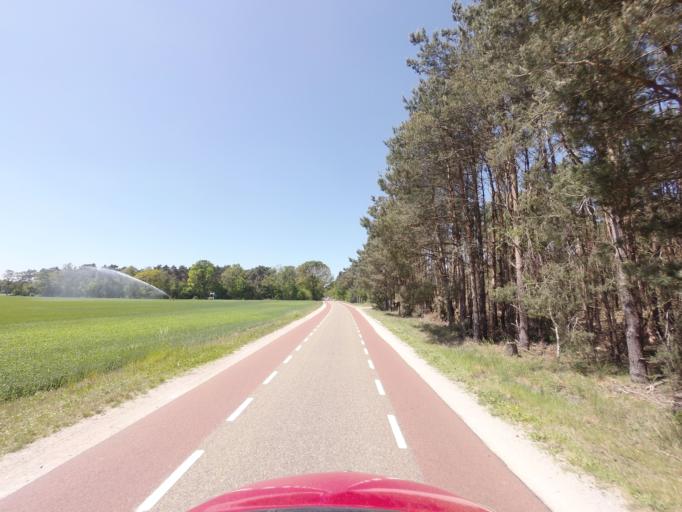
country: NL
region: North Brabant
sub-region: Gemeente Eersel
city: Eersel
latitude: 51.3097
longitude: 5.2814
